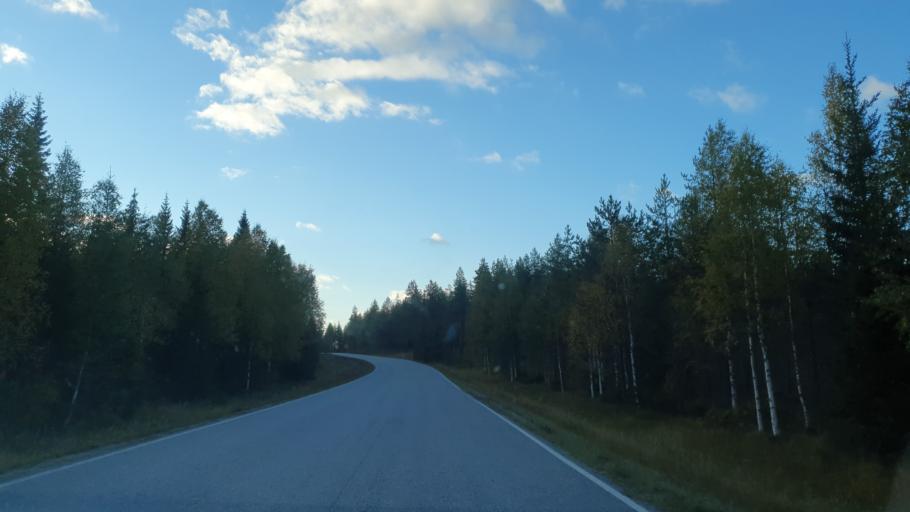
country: FI
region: Kainuu
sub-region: Kehys-Kainuu
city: Kuhmo
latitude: 63.9700
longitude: 29.6642
